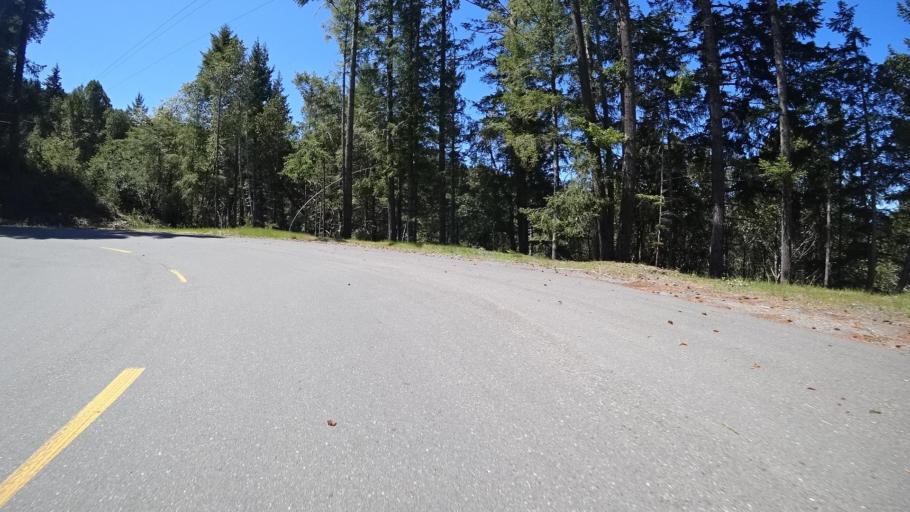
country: US
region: California
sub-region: Humboldt County
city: Rio Dell
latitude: 40.3275
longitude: -124.0458
